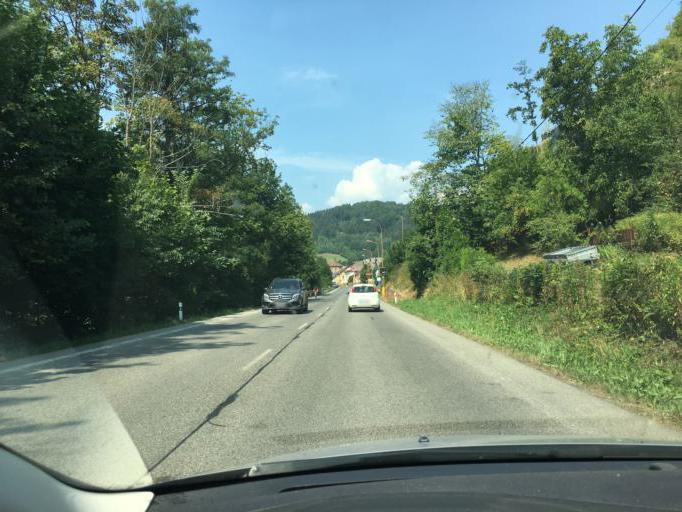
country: CZ
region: Liberecky
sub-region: Okres Semily
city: Ponikla
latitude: 50.6506
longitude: 15.4571
